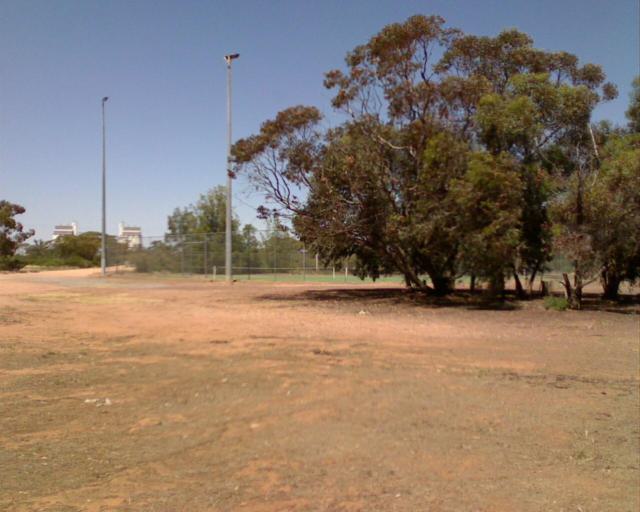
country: AU
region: South Australia
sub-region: Kimba
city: Caralue
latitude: -32.9428
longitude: 135.2769
